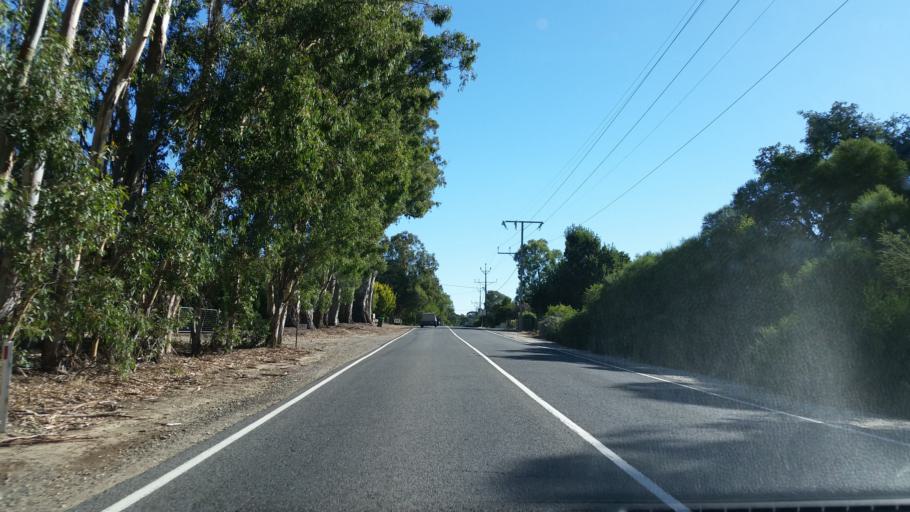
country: AU
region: South Australia
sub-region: Adelaide Hills
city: Birdwood
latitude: -34.8138
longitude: 138.9738
